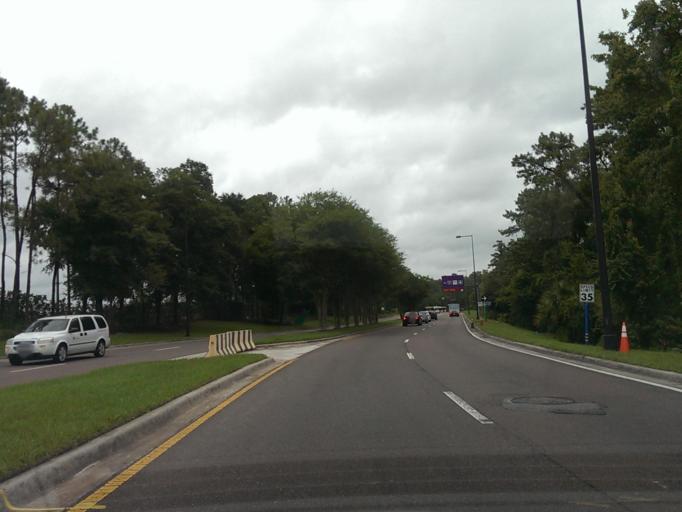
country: US
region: Florida
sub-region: Osceola County
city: Celebration
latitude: 28.3704
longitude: -81.5411
